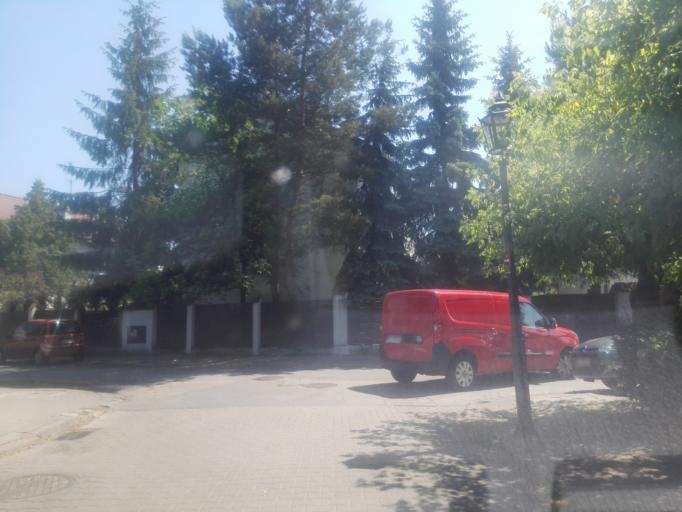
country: PL
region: Masovian Voivodeship
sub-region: Warszawa
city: Wilanow
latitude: 52.1889
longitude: 21.0685
